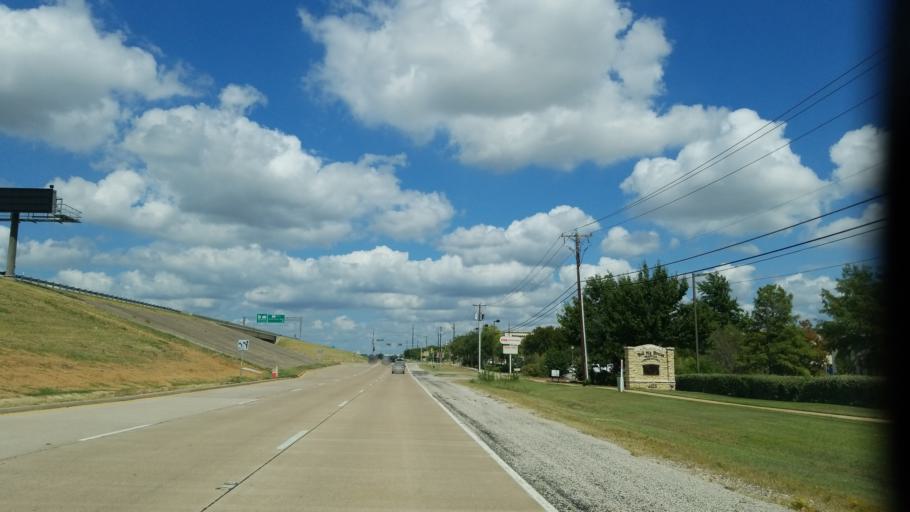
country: US
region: Texas
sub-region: Tarrant County
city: Grapevine
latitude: 32.8915
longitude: -97.0985
